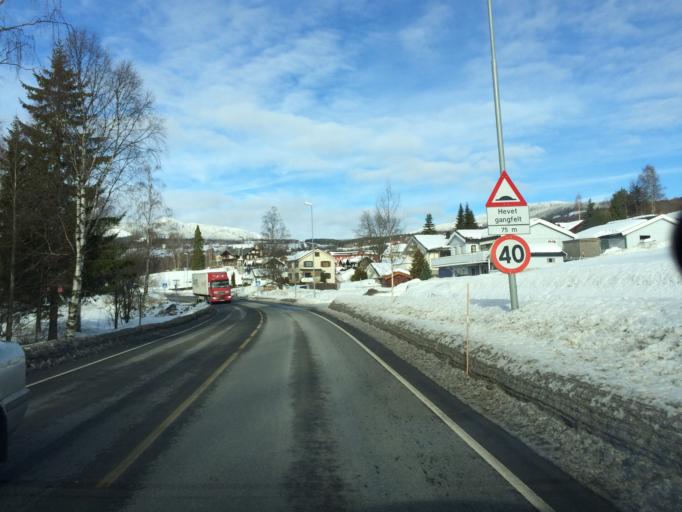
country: NO
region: Oppland
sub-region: Gausdal
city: Segalstad bru
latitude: 61.2129
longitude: 10.2926
